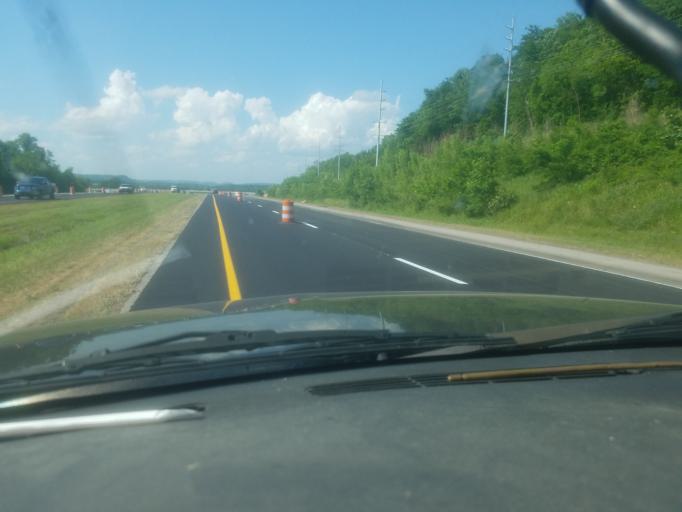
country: US
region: Tennessee
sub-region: Maury County
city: Mount Pleasant
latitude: 35.5375
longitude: -87.2213
